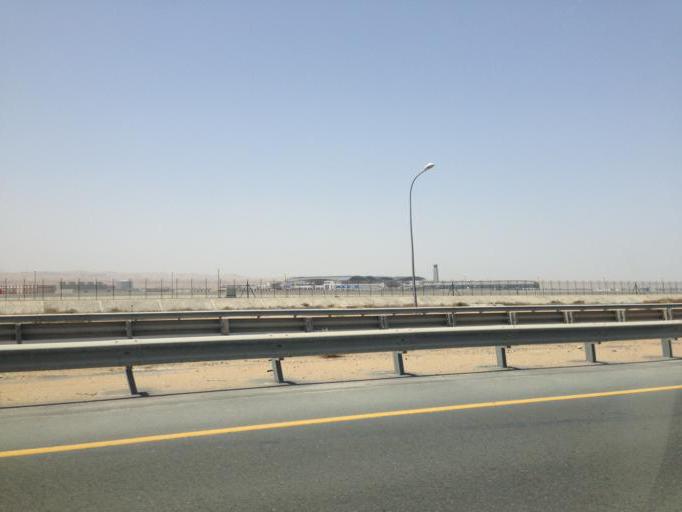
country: OM
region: Muhafazat Masqat
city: Bawshar
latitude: 23.6114
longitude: 58.3015
